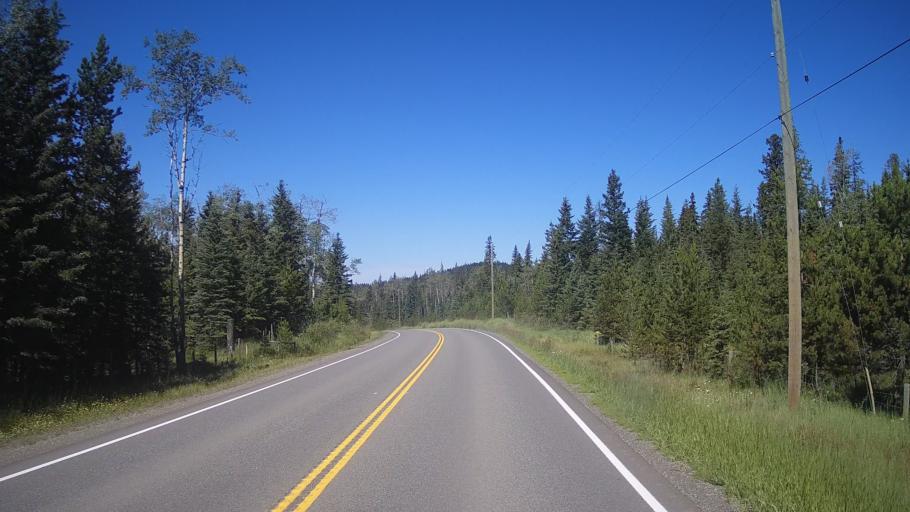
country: CA
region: British Columbia
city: Cache Creek
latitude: 51.5472
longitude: -121.0780
